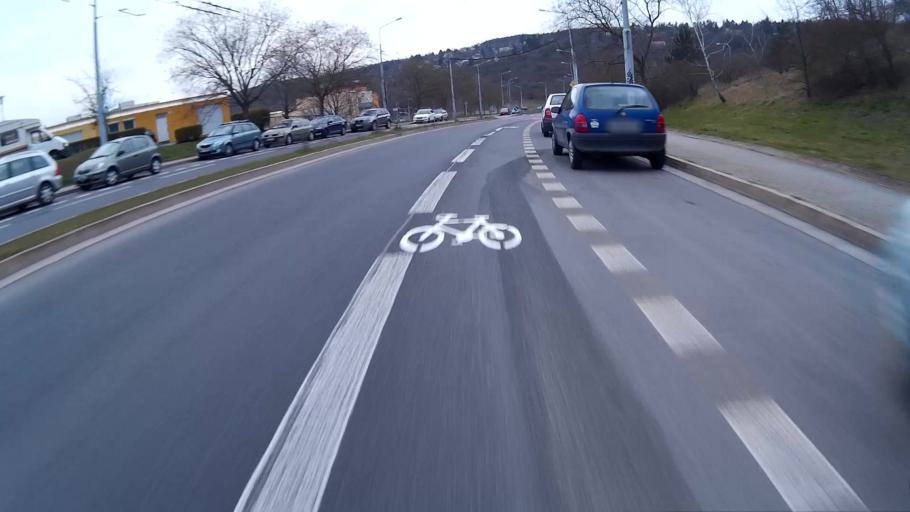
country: CZ
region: South Moravian
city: Ostopovice
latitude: 49.1780
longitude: 16.5516
